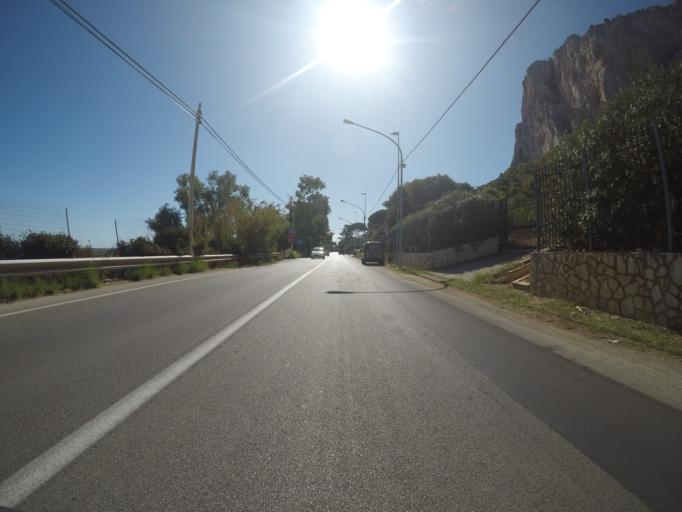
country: IT
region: Sicily
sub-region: Palermo
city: Palermo
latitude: 38.1855
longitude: 13.3619
